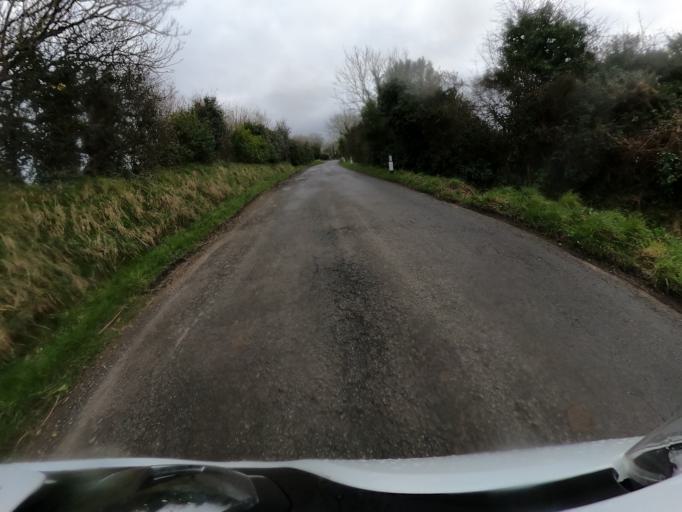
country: IM
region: Ramsey
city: Ramsey
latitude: 54.3778
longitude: -4.4473
